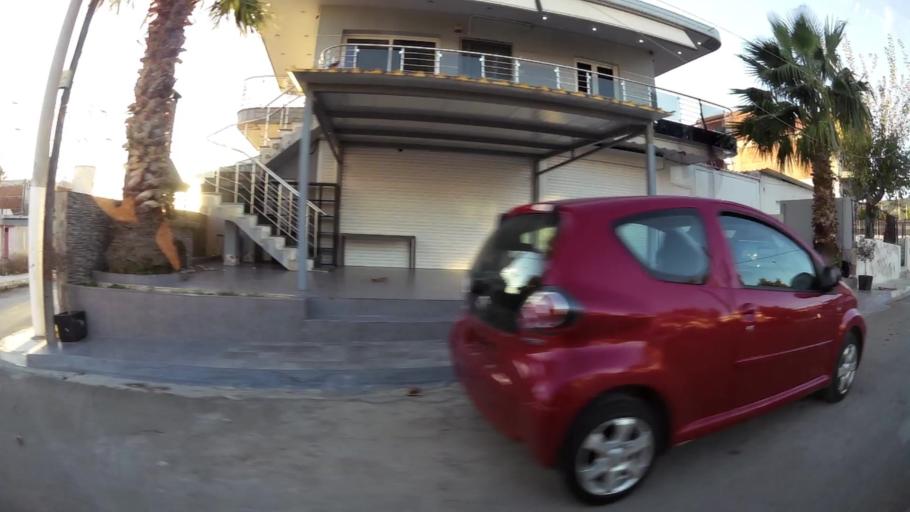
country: GR
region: Attica
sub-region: Nomarchia Dytikis Attikis
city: Ano Liosia
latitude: 38.0901
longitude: 23.6898
